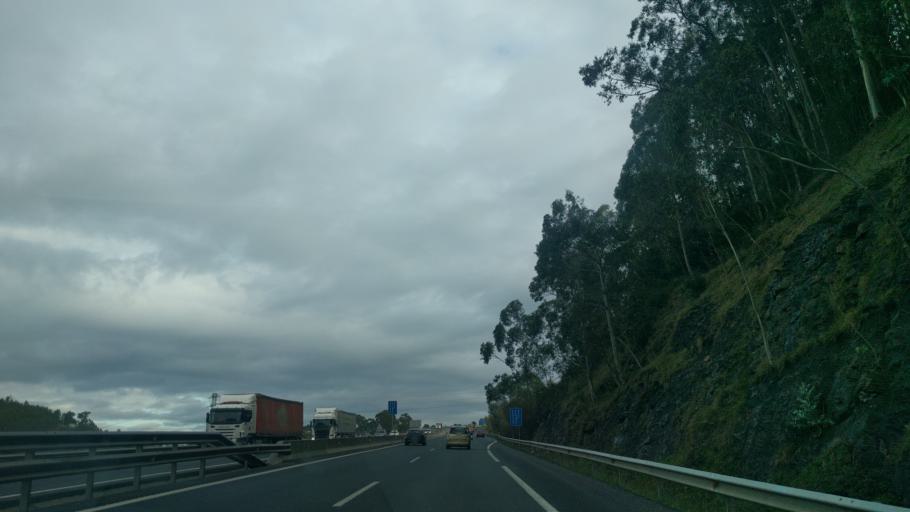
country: ES
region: Cantabria
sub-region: Provincia de Cantabria
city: Castro-Urdiales
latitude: 43.3540
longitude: -3.2007
